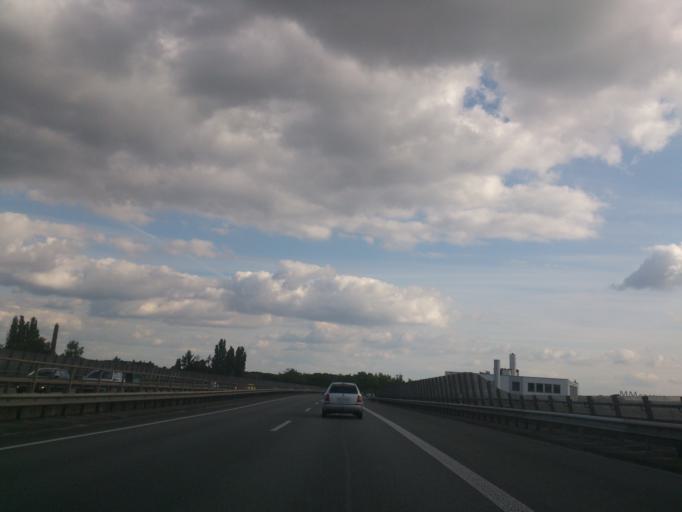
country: DE
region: North Rhine-Westphalia
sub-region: Regierungsbezirk Detmold
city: Bielefeld
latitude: 51.9919
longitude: 8.4949
